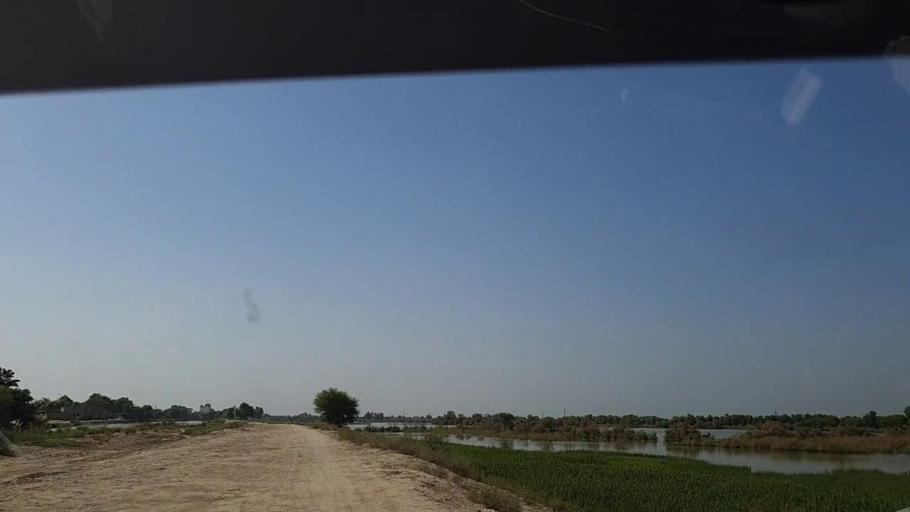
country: PK
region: Sindh
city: Ghauspur
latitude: 28.1779
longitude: 69.0919
